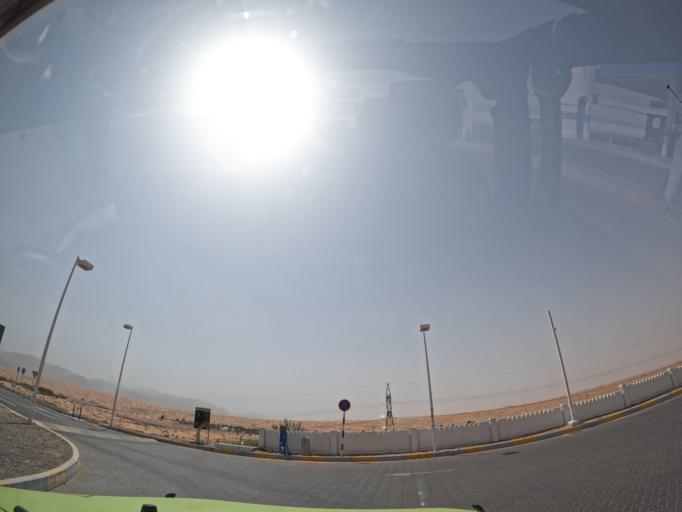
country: OM
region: Al Buraimi
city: Al Buraymi
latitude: 24.7417
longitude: 55.8010
